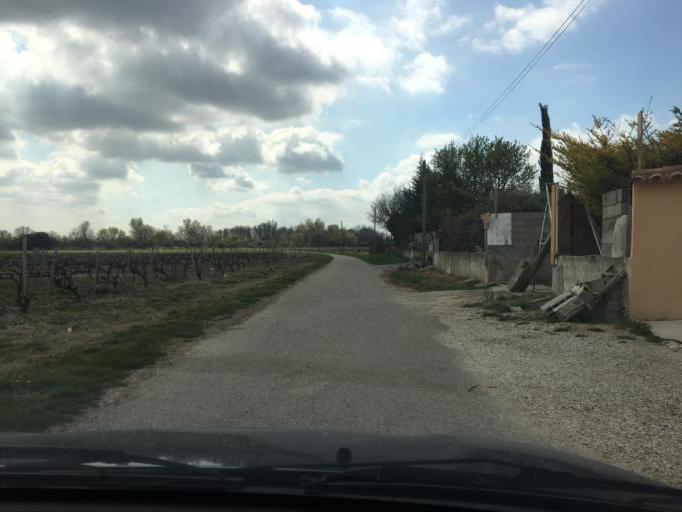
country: FR
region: Provence-Alpes-Cote d'Azur
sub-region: Departement du Vaucluse
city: Serignan-du-Comtat
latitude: 44.1790
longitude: 4.8349
